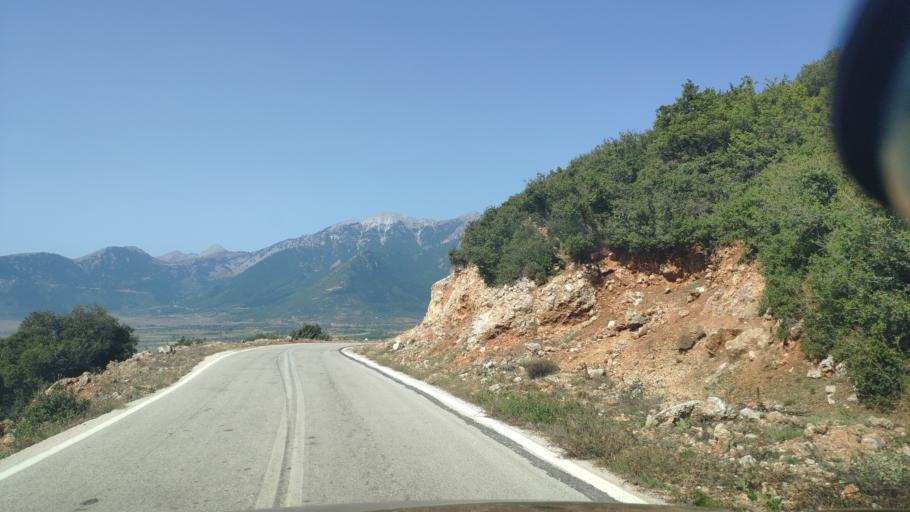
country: GR
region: West Greece
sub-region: Nomos Achaias
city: Aiyira
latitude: 37.8789
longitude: 22.3527
